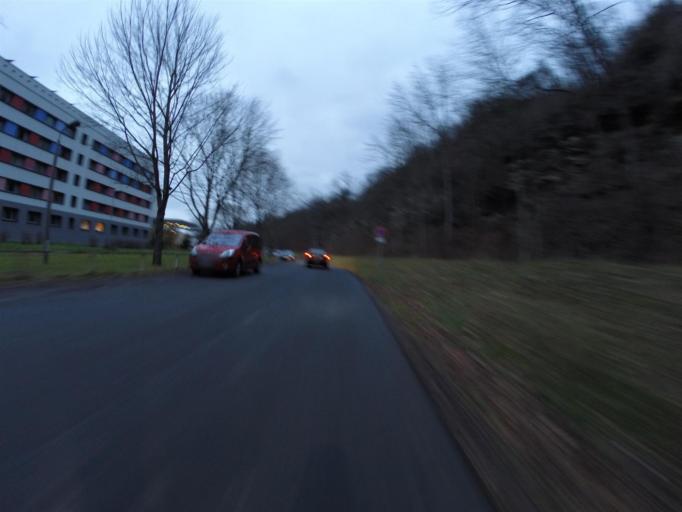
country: DE
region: Thuringia
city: Jena
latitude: 50.9156
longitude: 11.5914
